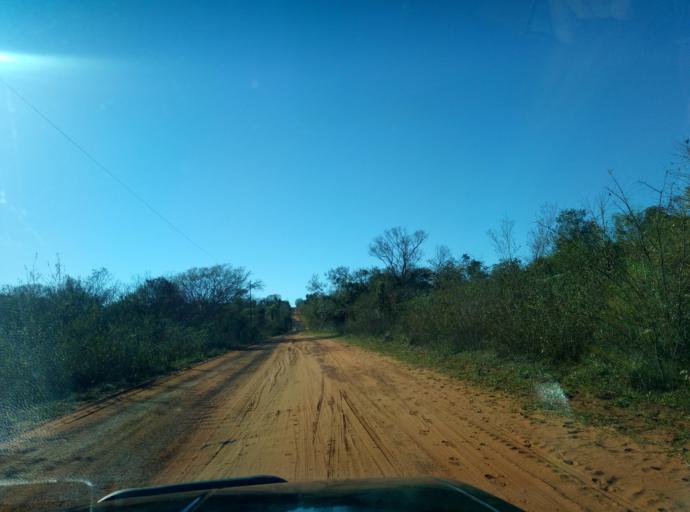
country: PY
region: Caaguazu
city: Carayao
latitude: -25.1571
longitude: -56.3004
